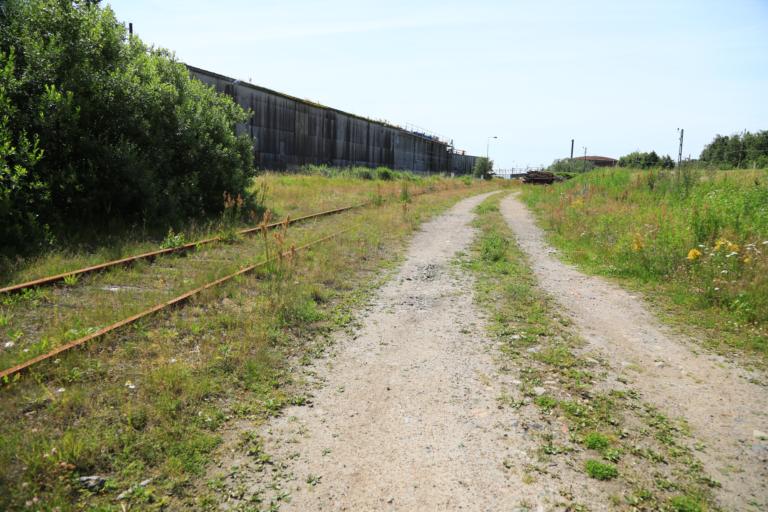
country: SE
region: Halland
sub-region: Varbergs Kommun
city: Varberg
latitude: 57.1194
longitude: 12.2543
